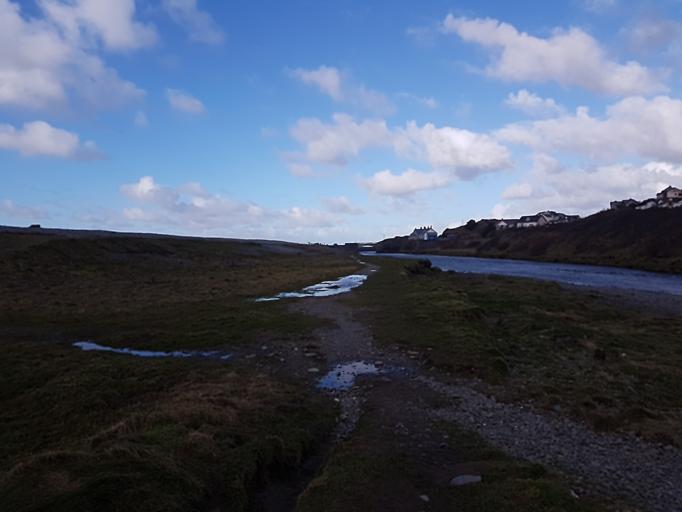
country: GB
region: Wales
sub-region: County of Ceredigion
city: Penparcau
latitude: 52.4025
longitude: -4.0879
